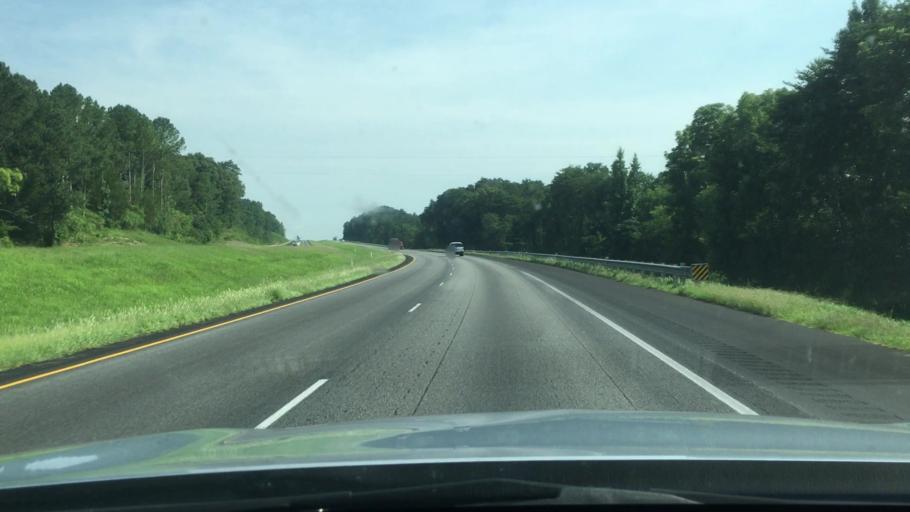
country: US
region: Georgia
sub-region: Dade County
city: Trenton
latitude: 34.7339
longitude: -85.5380
